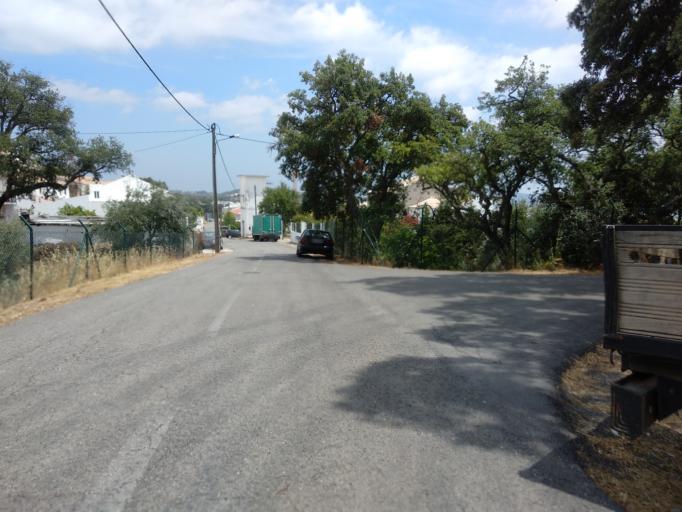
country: PT
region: Faro
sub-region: Sao Bras de Alportel
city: Sao Bras de Alportel
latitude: 37.1628
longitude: -7.8889
